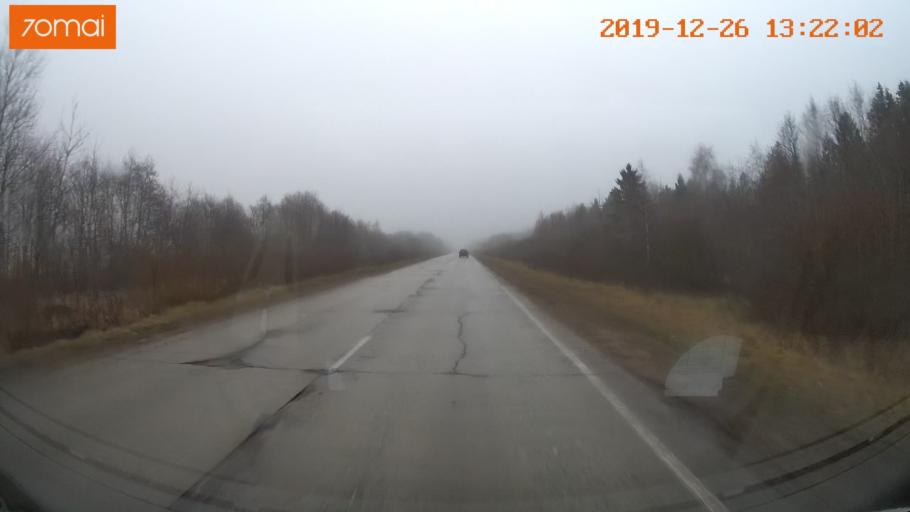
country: RU
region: Vologda
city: Cherepovets
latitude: 58.9064
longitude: 38.1665
